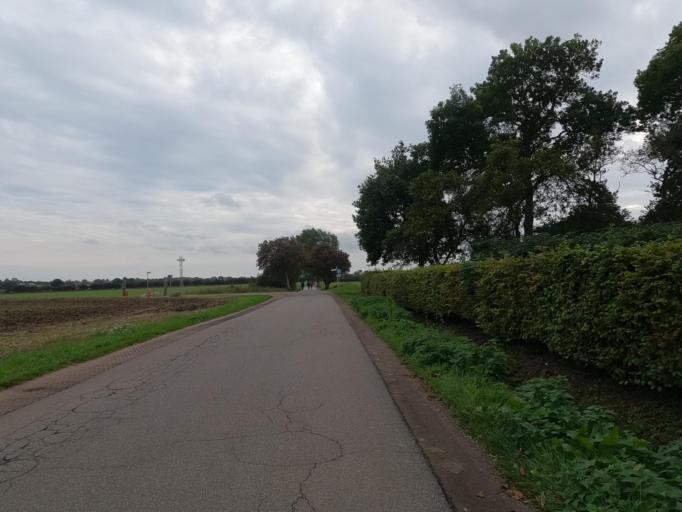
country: DE
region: Schleswig-Holstein
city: Neukirchen
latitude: 54.3447
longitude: 11.0496
